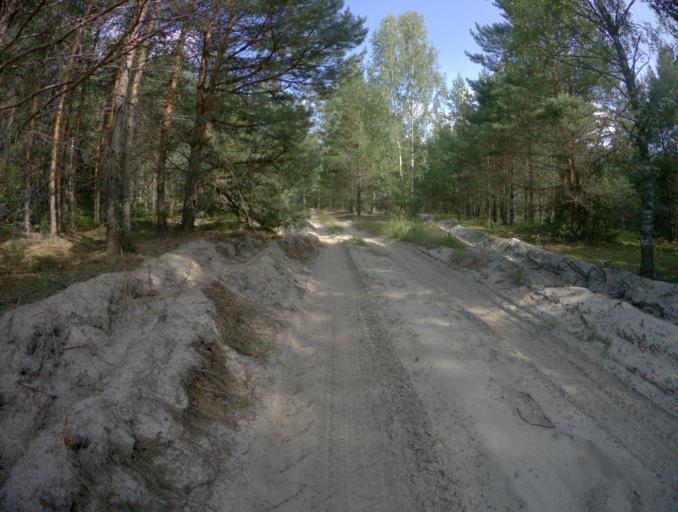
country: RU
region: Vladimir
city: Vorsha
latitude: 55.9094
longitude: 40.1633
